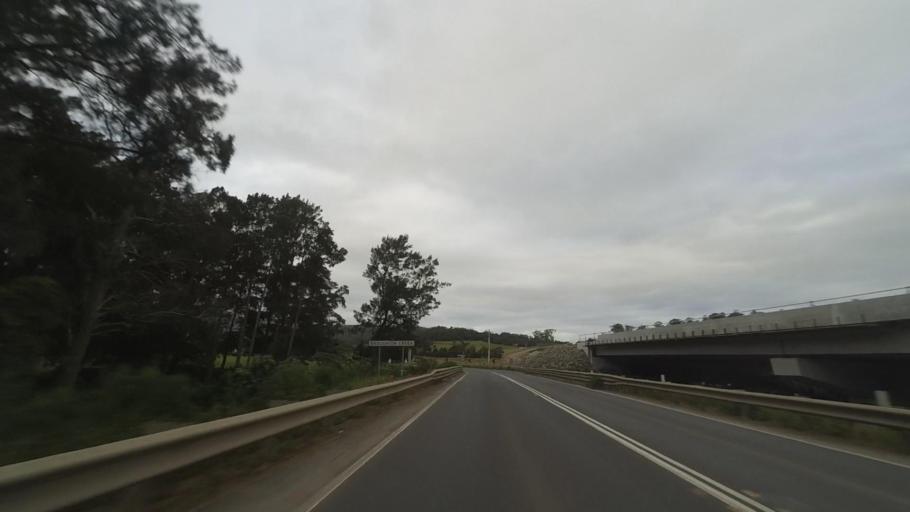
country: AU
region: New South Wales
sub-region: Kiama
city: Gerringong
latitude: -34.7455
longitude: 150.7592
